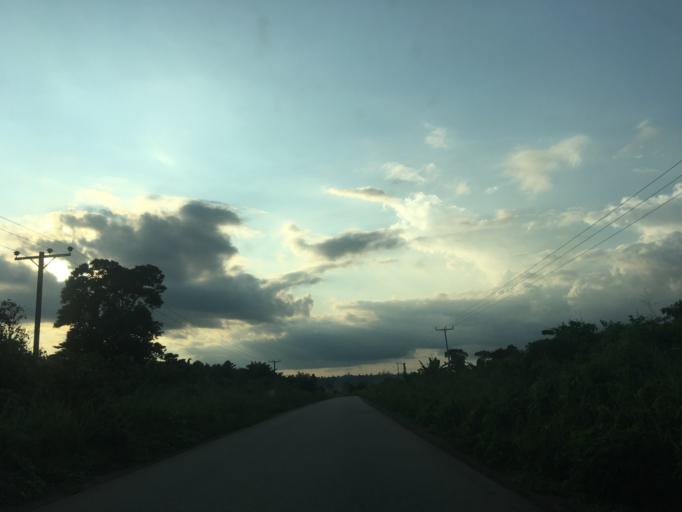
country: GH
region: Western
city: Bibiani
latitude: 6.6297
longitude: -2.4159
